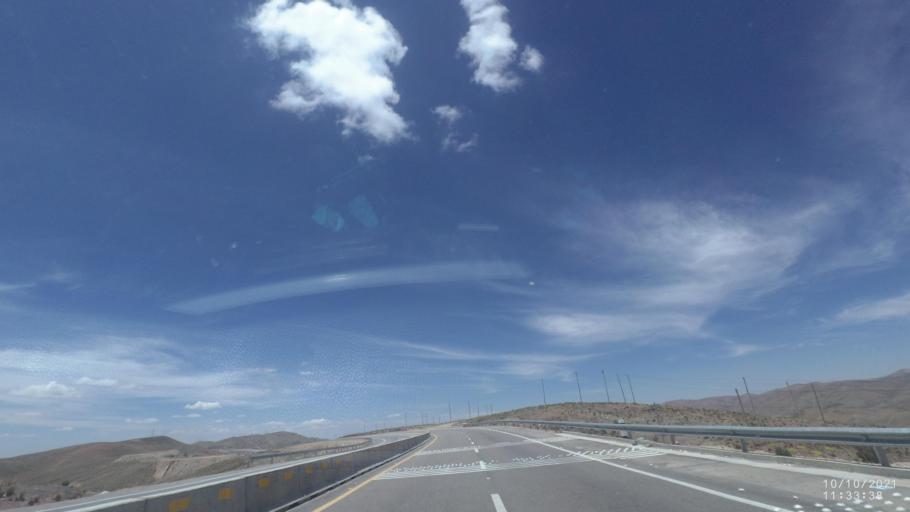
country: BO
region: Cochabamba
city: Colchani
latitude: -17.6458
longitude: -66.8440
